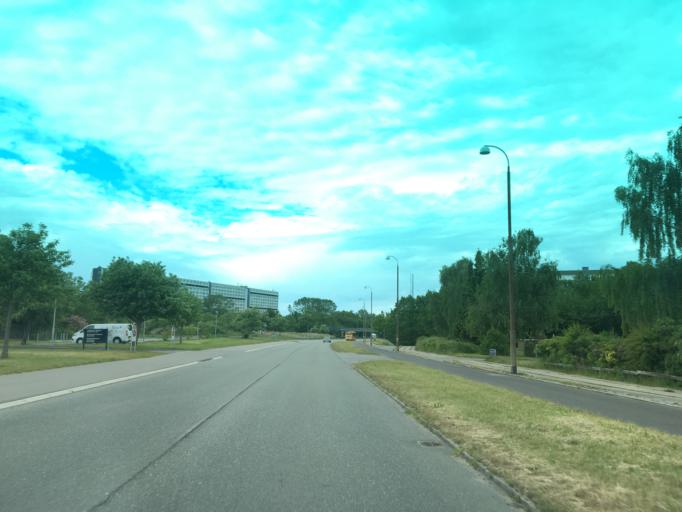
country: DK
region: Capital Region
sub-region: Hvidovre Kommune
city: Hvidovre
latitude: 55.6230
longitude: 12.4591
